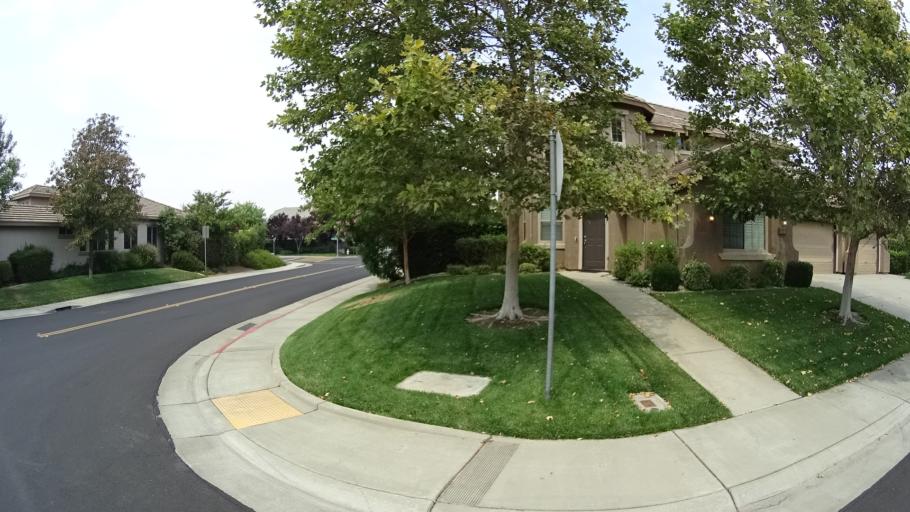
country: US
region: California
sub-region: Sacramento County
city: Laguna
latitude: 38.3826
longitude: -121.4272
